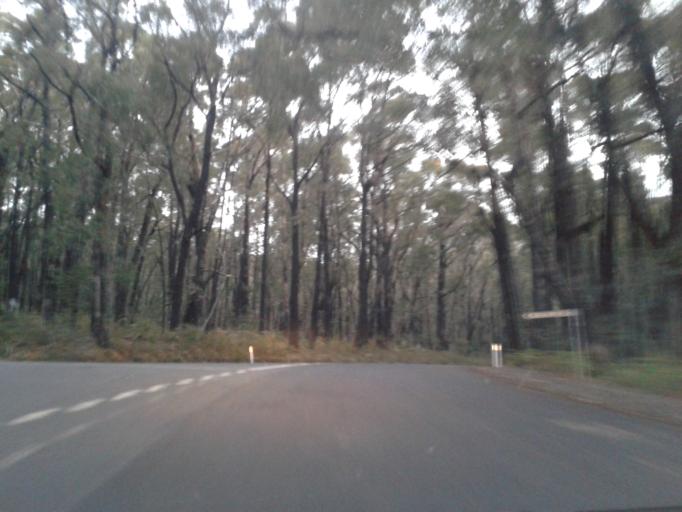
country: AU
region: Victoria
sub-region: Northern Grampians
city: Stawell
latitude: -37.1749
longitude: 142.5053
